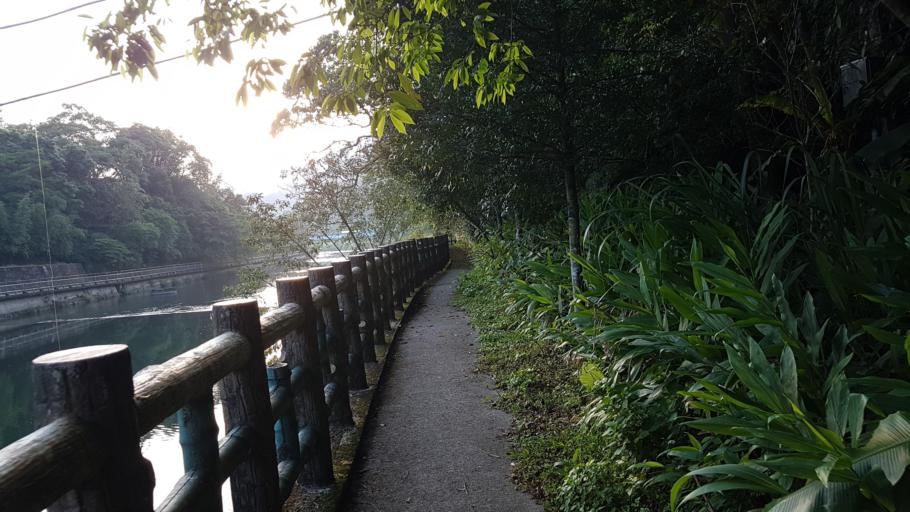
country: TW
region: Taiwan
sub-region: Yilan
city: Yilan
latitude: 24.9336
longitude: 121.7033
